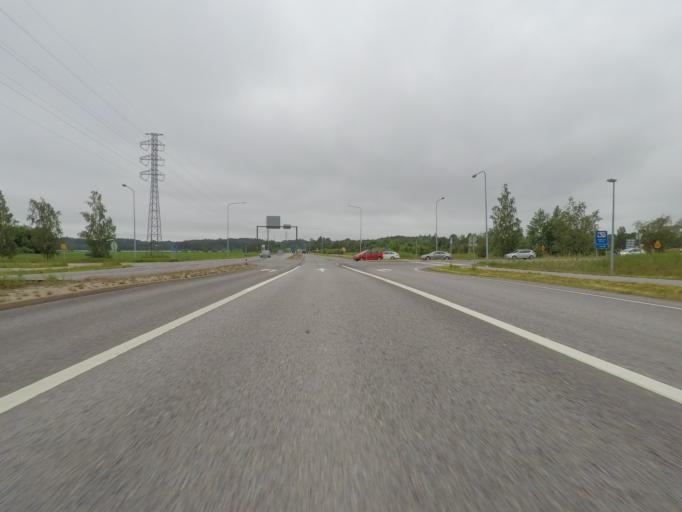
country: FI
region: Varsinais-Suomi
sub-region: Turku
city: Naantali
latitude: 60.4737
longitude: 22.0531
